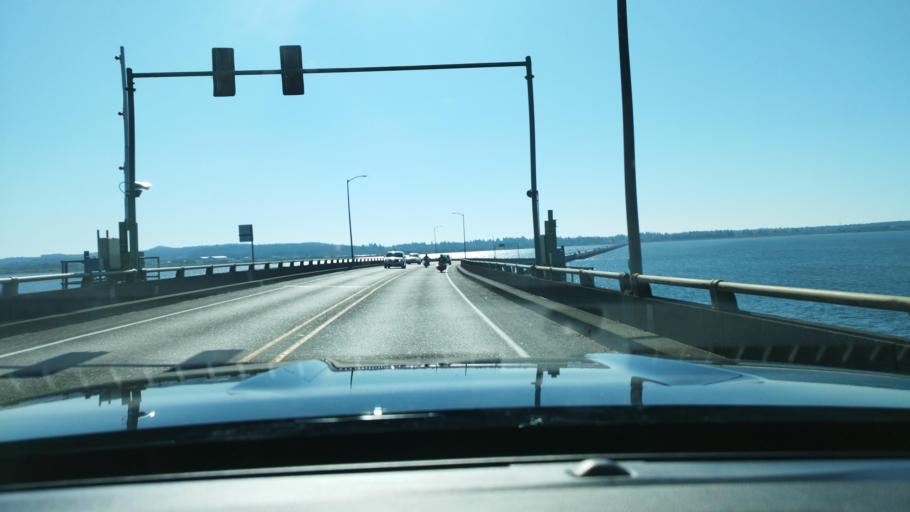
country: US
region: Oregon
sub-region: Clatsop County
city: Astoria
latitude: 46.1756
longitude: -123.8680
